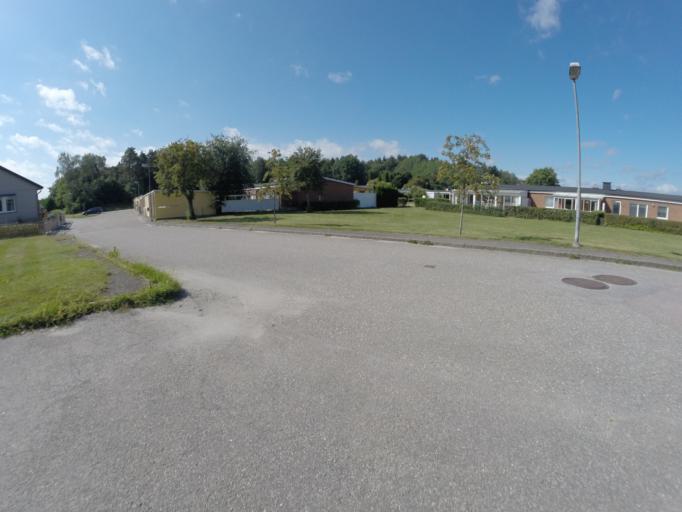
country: SE
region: Soedermanland
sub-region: Eskilstuna Kommun
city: Torshalla
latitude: 59.4181
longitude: 16.4848
